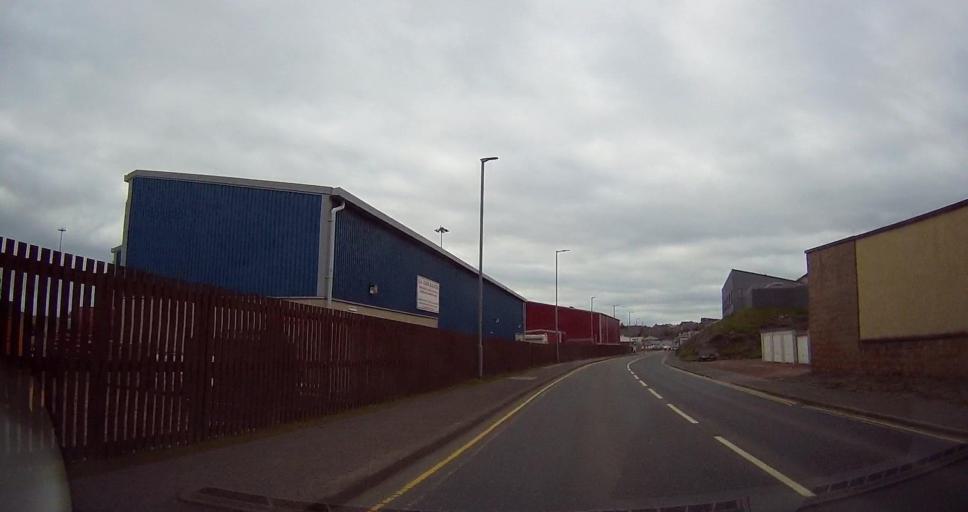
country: GB
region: Scotland
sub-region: Shetland Islands
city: Lerwick
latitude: 60.1618
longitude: -1.1585
